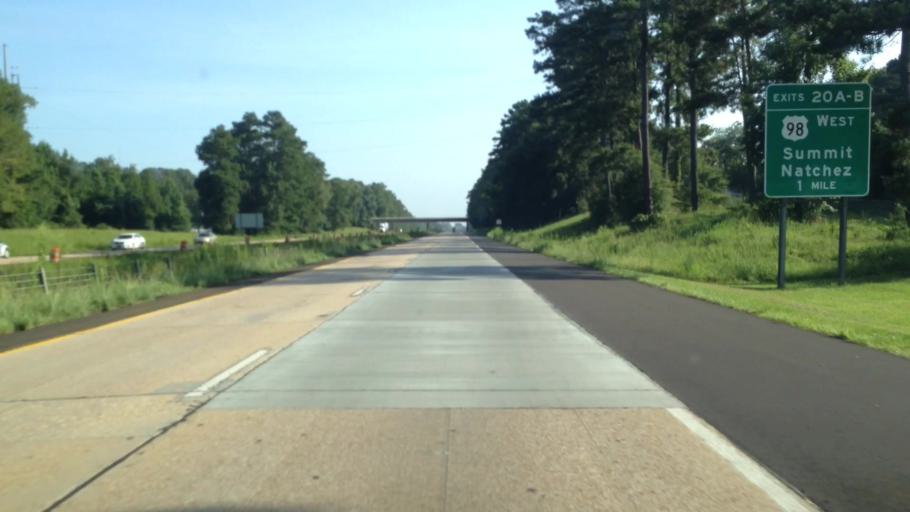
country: US
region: Mississippi
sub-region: Pike County
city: Summit
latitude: 31.2694
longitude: -90.4789
